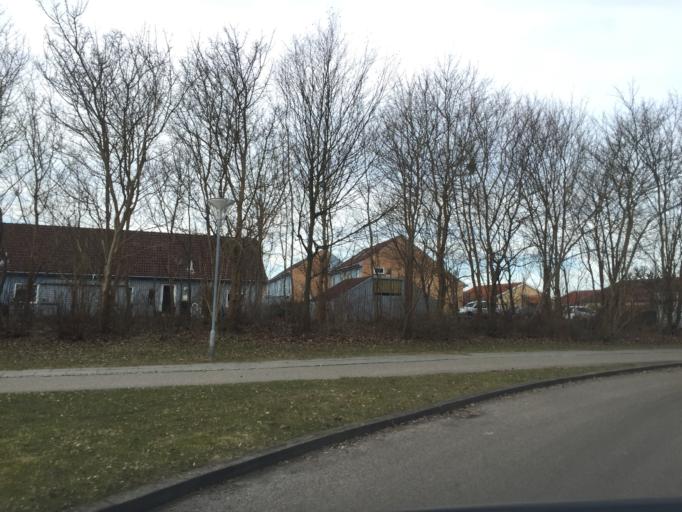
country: DK
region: Capital Region
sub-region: Fureso Kommune
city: Farum
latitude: 55.8153
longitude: 12.3512
